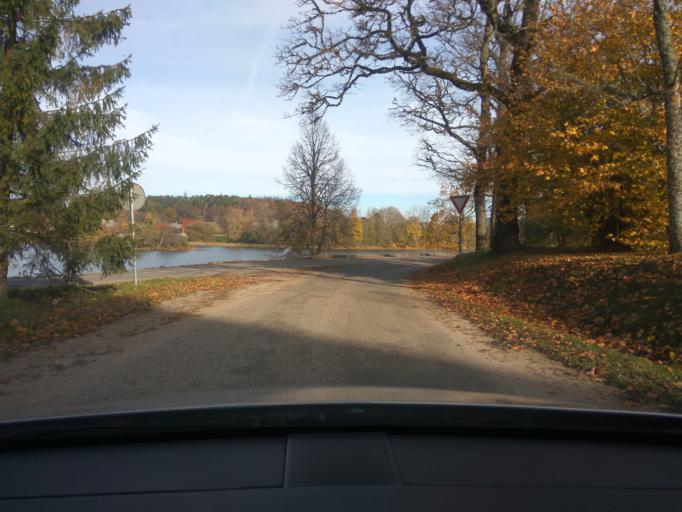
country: LV
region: Alsunga
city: Alsunga
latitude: 57.0177
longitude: 21.6896
